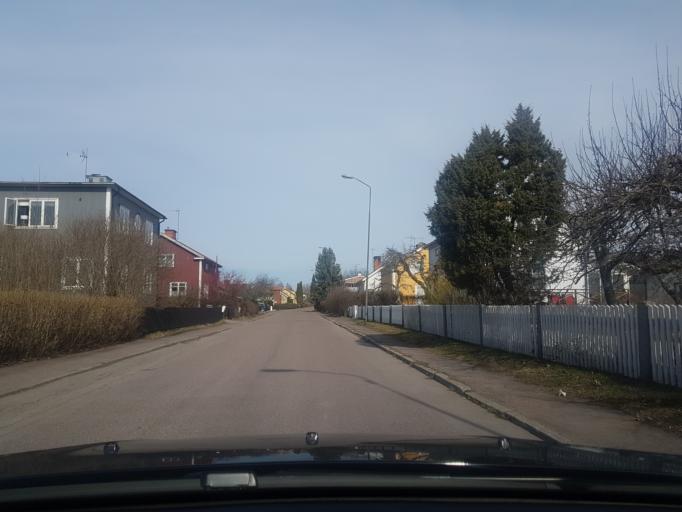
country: SE
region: Dalarna
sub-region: Borlange Kommun
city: Borlaenge
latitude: 60.4897
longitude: 15.4174
